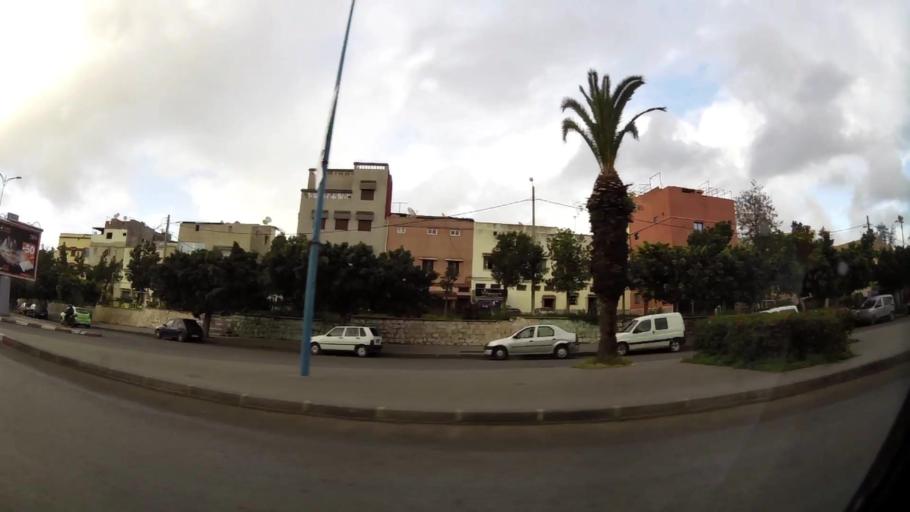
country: MA
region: Grand Casablanca
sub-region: Mohammedia
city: Mohammedia
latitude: 33.6879
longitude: -7.3917
